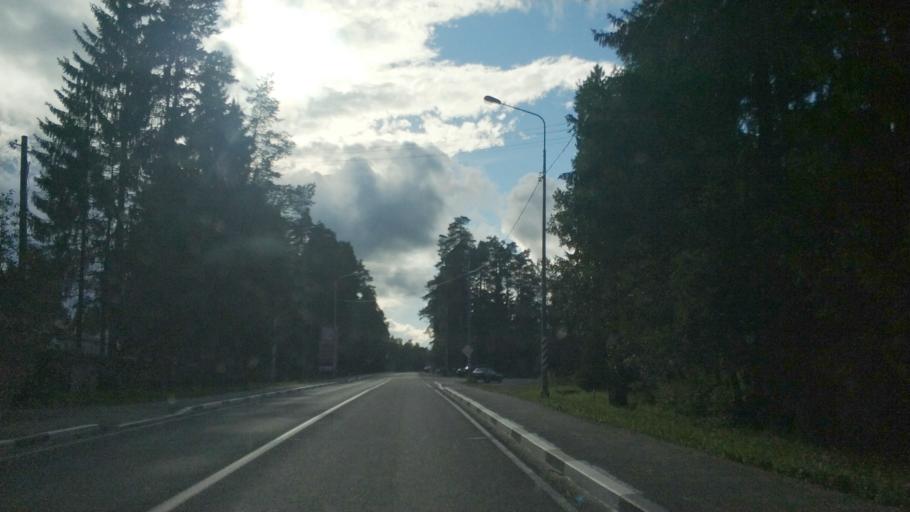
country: RU
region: Republic of Karelia
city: Lakhdenpokh'ya
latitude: 61.5170
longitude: 30.1456
